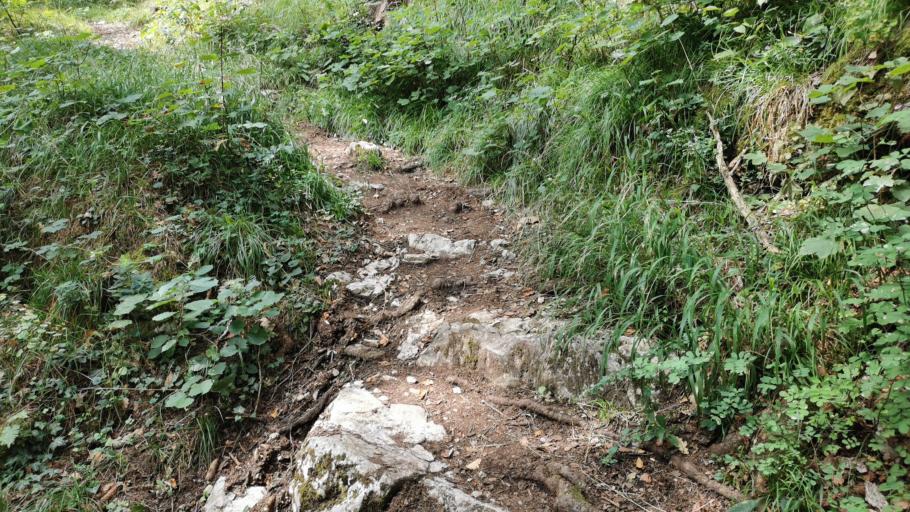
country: FR
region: Rhone-Alpes
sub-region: Departement de la Haute-Savoie
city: Sevrier
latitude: 45.8662
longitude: 6.1346
